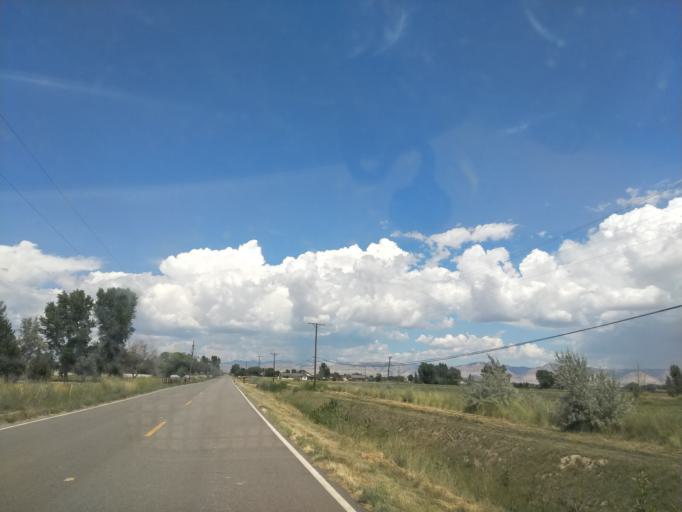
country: US
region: Colorado
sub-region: Mesa County
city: Redlands
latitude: 39.1322
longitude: -108.6640
